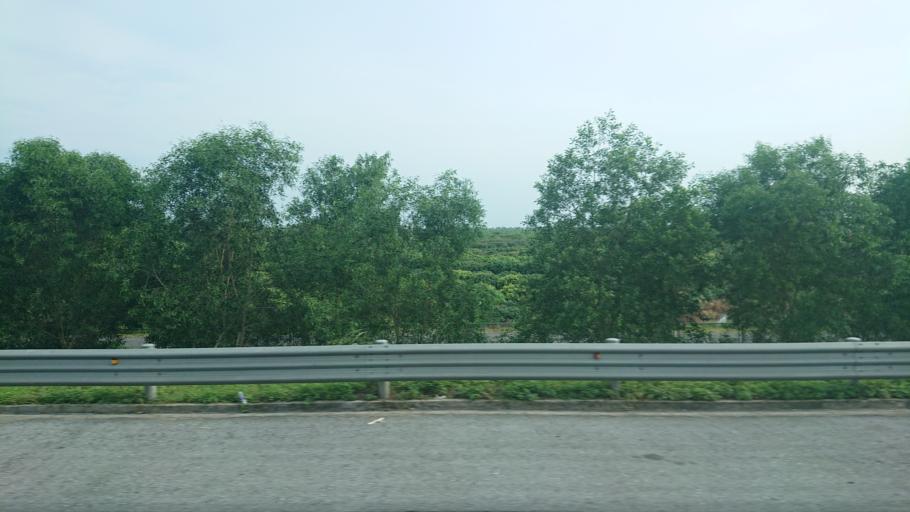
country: VN
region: Hai Duong
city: Tu Ky
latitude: 20.8195
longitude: 106.4807
